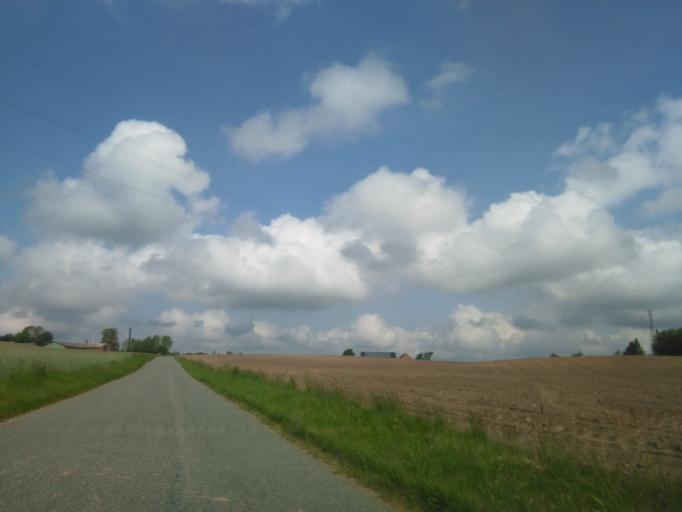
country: DK
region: Central Jutland
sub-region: Arhus Kommune
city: Sabro
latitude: 56.1980
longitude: 9.9996
